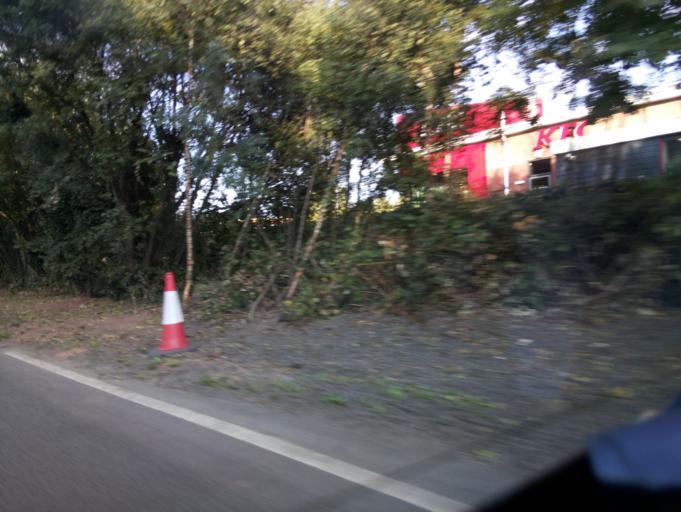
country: GB
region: Wales
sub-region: Torfaen County Borough
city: New Inn
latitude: 51.6925
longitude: -3.0220
